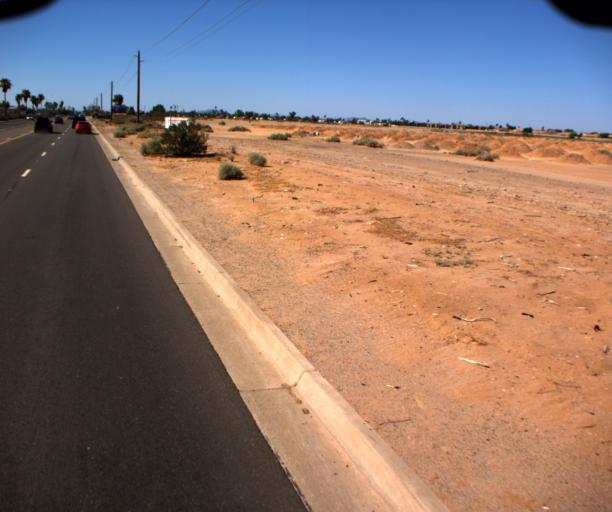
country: US
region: Arizona
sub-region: Pinal County
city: Casa Grande
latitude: 32.9047
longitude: -111.7574
